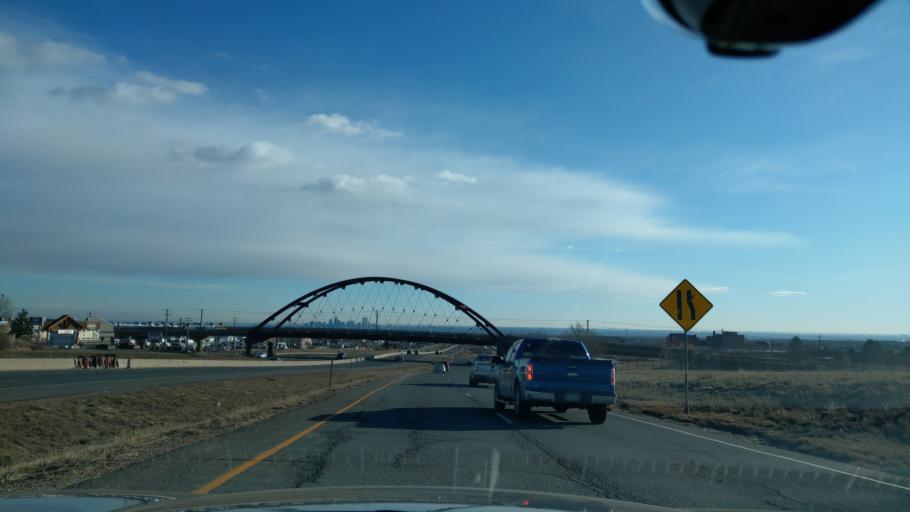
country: US
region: Colorado
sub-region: Jefferson County
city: Applewood
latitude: 39.7251
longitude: -105.1282
